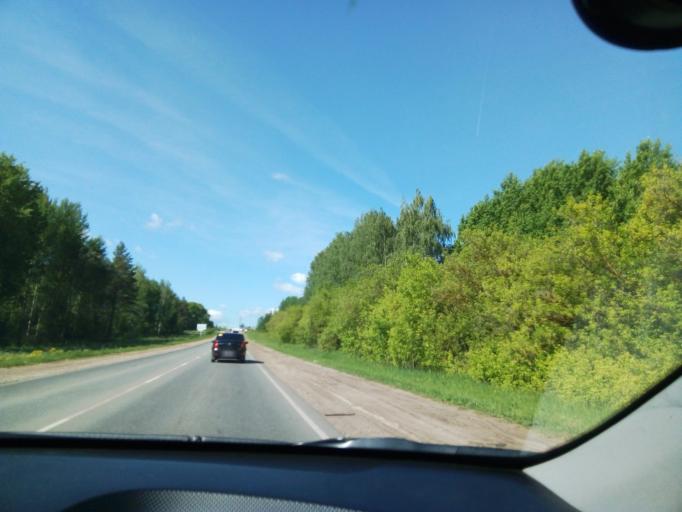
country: RU
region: Chuvashia
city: Novocheboksarsk
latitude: 56.0797
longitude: 47.5010
